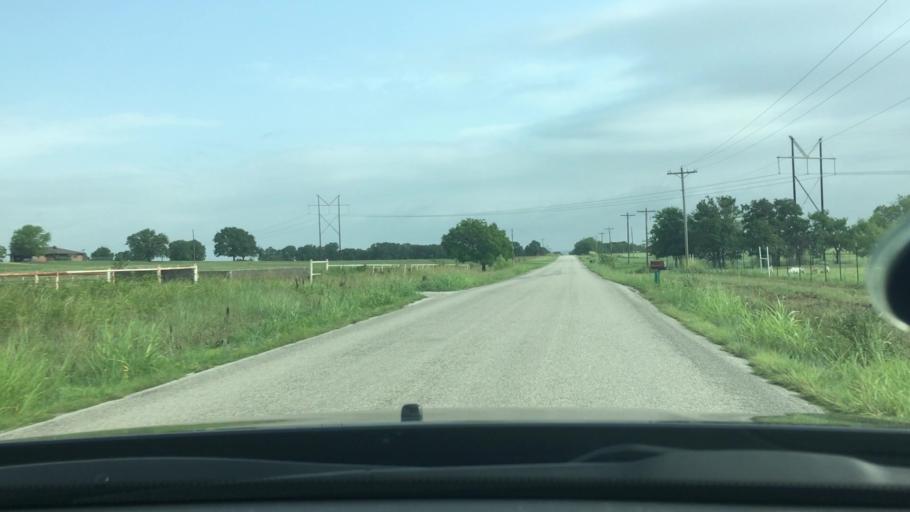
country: US
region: Oklahoma
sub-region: Carter County
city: Lone Grove
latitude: 34.2262
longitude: -97.2737
